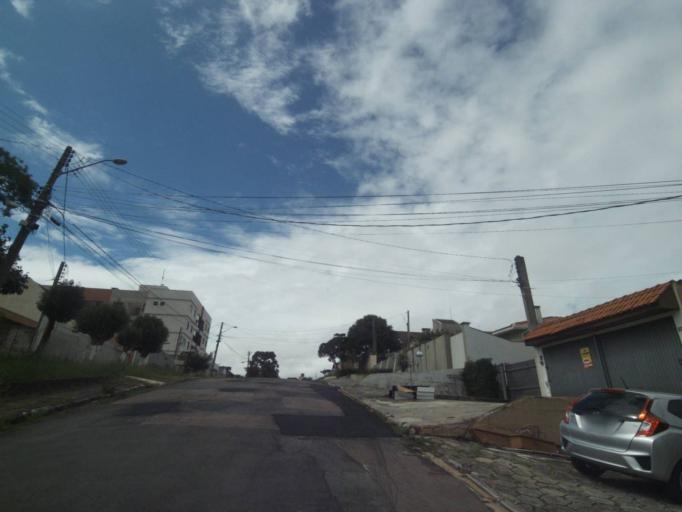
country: BR
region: Parana
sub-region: Curitiba
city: Curitiba
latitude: -25.4816
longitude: -49.2839
